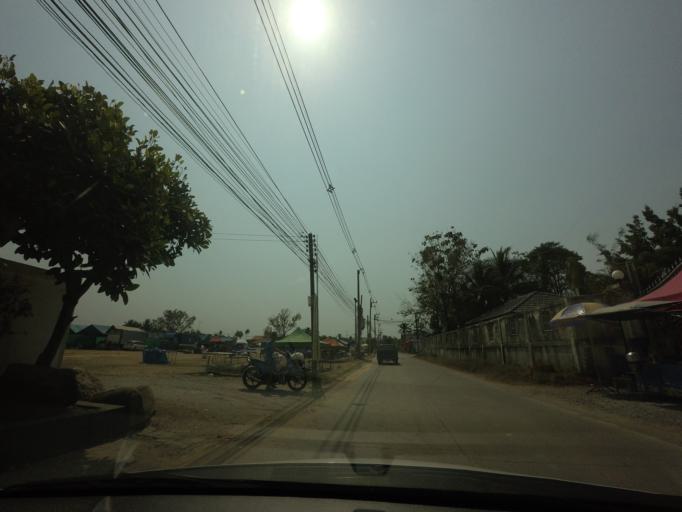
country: TH
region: Nakhon Pathom
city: Sam Phran
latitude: 13.7606
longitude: 100.2469
